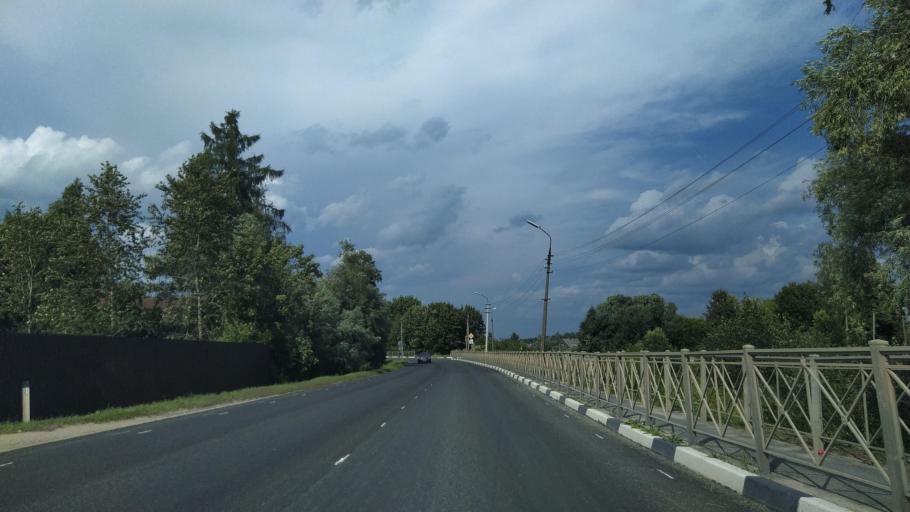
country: RU
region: Pskov
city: Porkhov
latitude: 57.7684
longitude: 29.5525
